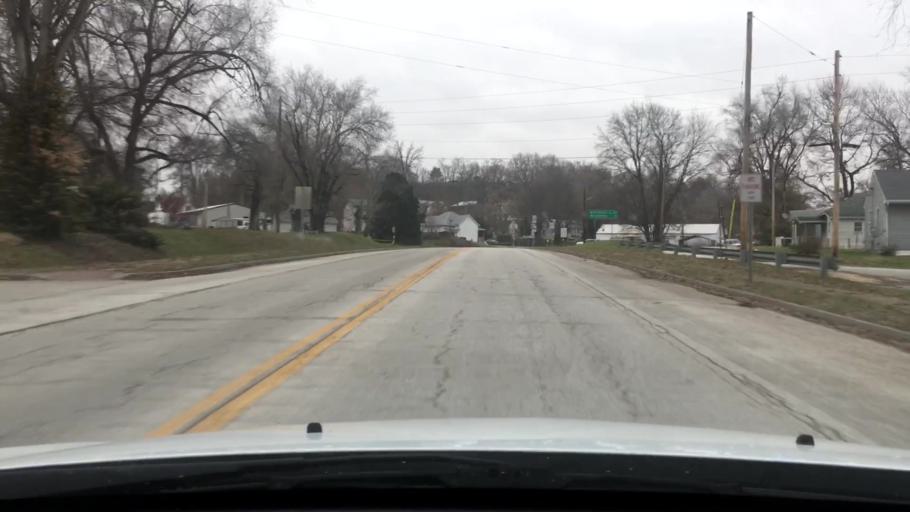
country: US
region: Missouri
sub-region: Pike County
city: Louisiana
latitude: 39.4532
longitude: -91.0568
